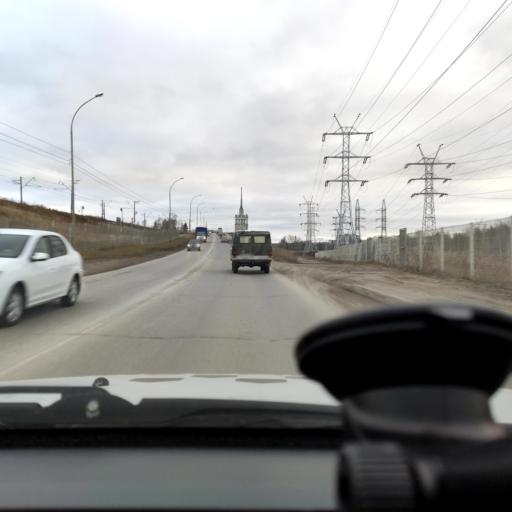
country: RU
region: Perm
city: Perm
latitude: 58.1149
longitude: 56.3347
